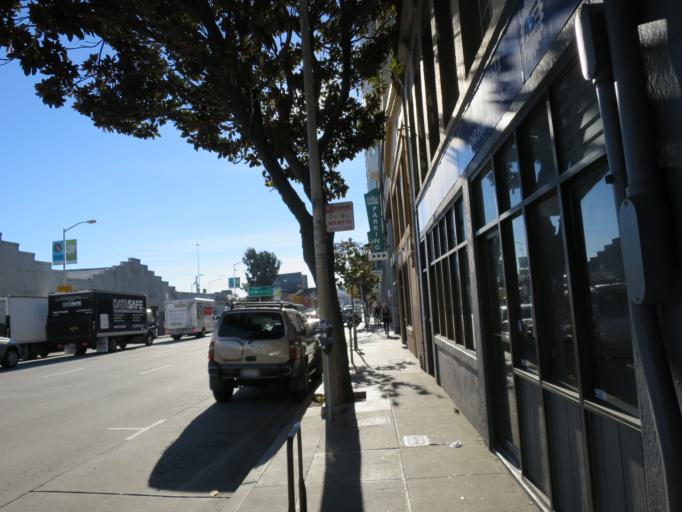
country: US
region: California
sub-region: San Francisco County
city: San Francisco
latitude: 37.7814
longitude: -122.3990
